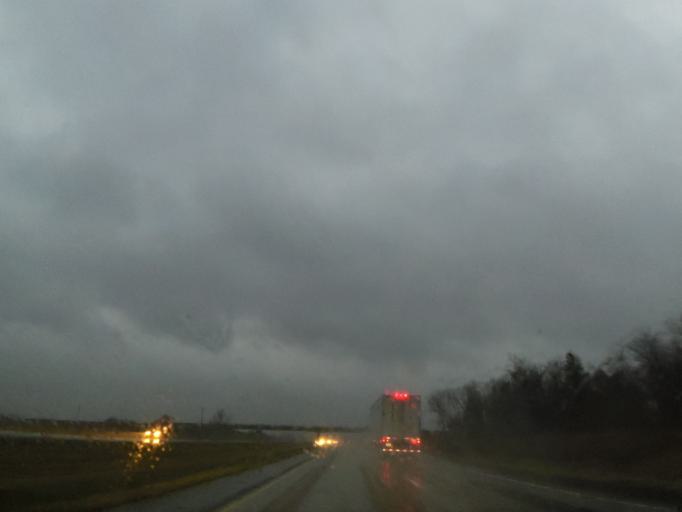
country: US
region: Iowa
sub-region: Worth County
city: Northwood
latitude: 43.4746
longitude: -93.3508
